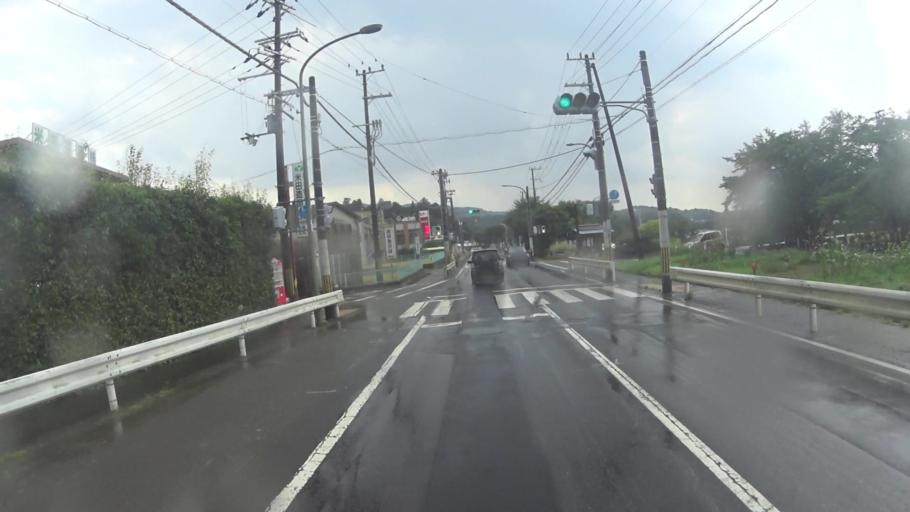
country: JP
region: Kyoto
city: Uji
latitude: 34.8563
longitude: 135.8671
